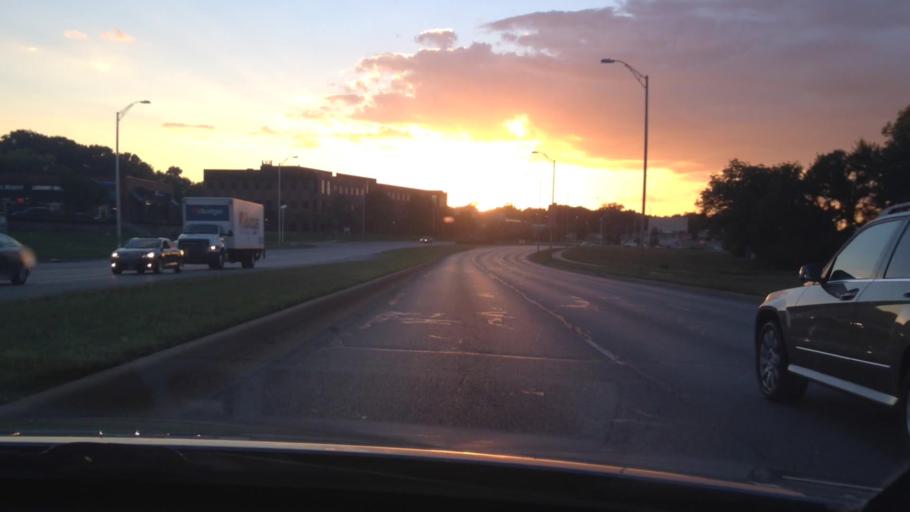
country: US
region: Missouri
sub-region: Jackson County
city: Raytown
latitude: 39.0348
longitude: -94.5341
